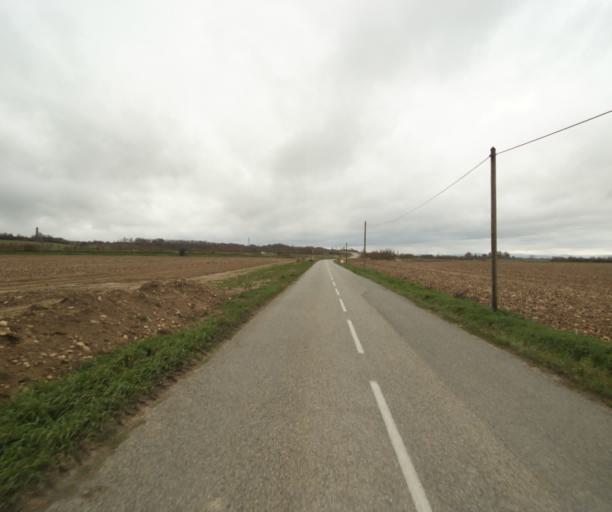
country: FR
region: Midi-Pyrenees
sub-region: Departement de l'Ariege
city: Saverdun
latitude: 43.2022
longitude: 1.6276
